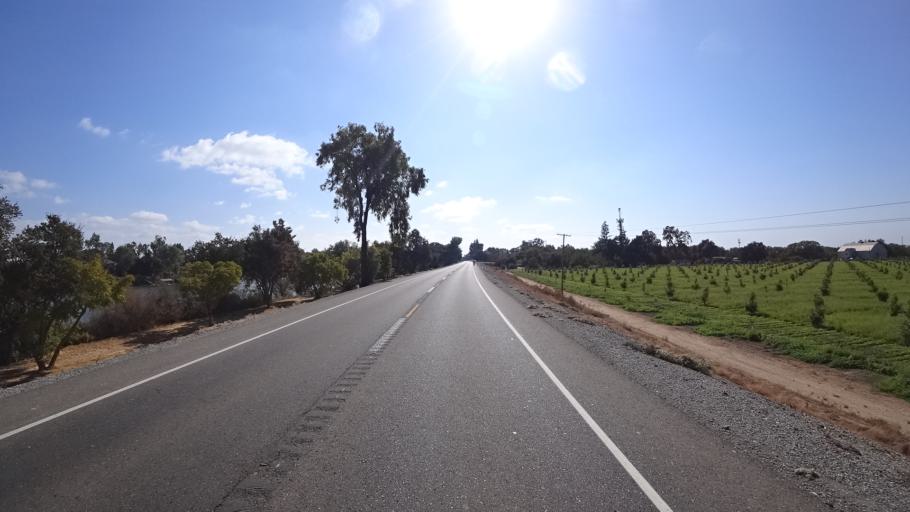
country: US
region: California
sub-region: Yolo County
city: West Sacramento
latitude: 38.6274
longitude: -121.5639
